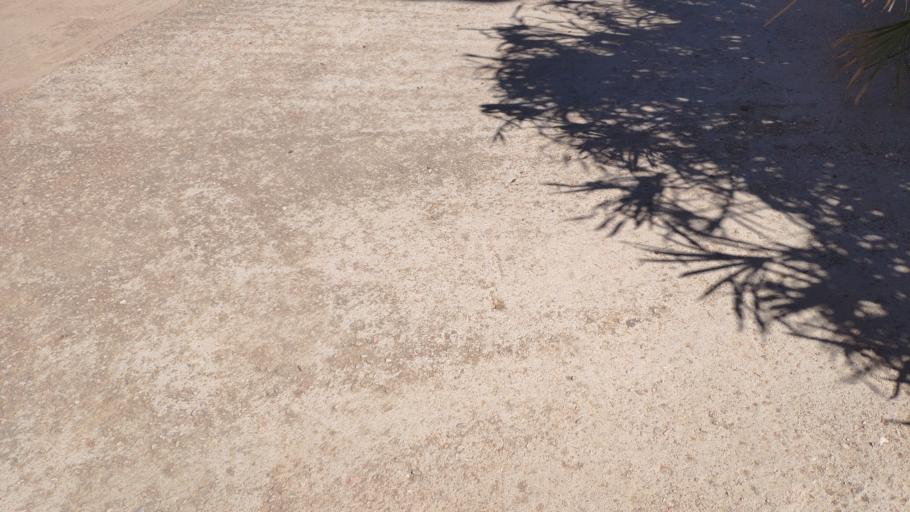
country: GR
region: Attica
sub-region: Nomarchia Anatolikis Attikis
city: Spata
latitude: 37.9804
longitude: 23.9105
